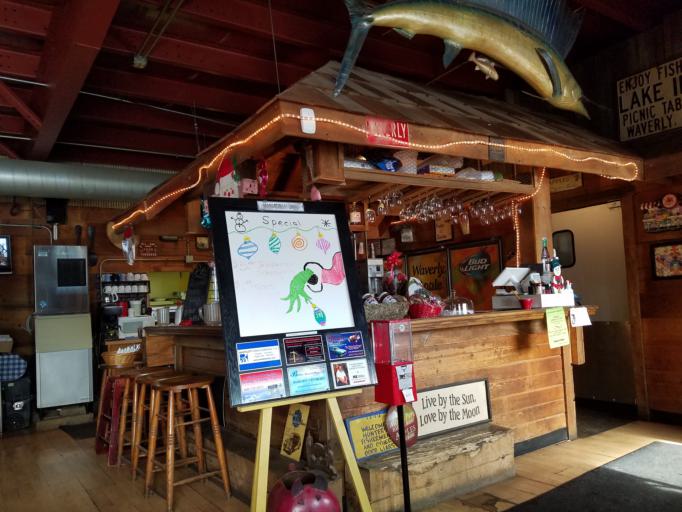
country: US
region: Missouri
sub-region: Carroll County
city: Carrollton
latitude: 39.1965
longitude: -93.5307
